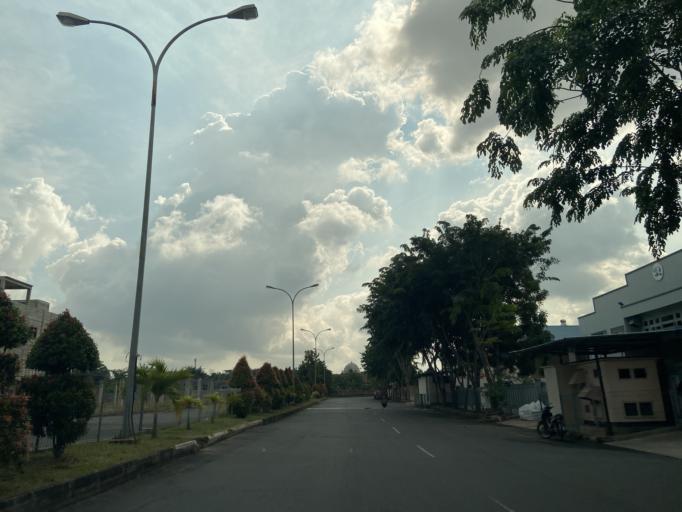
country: SG
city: Singapore
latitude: 1.1110
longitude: 104.0737
